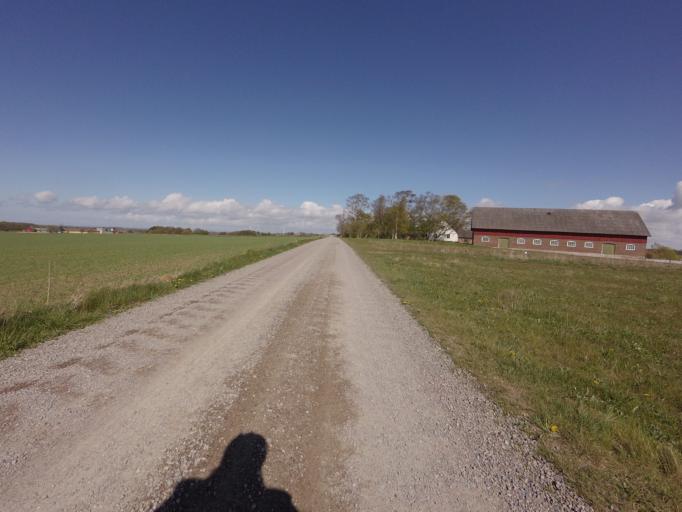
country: DK
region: Capital Region
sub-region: Helsingor Kommune
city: Helsingor
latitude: 56.1281
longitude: 12.6295
